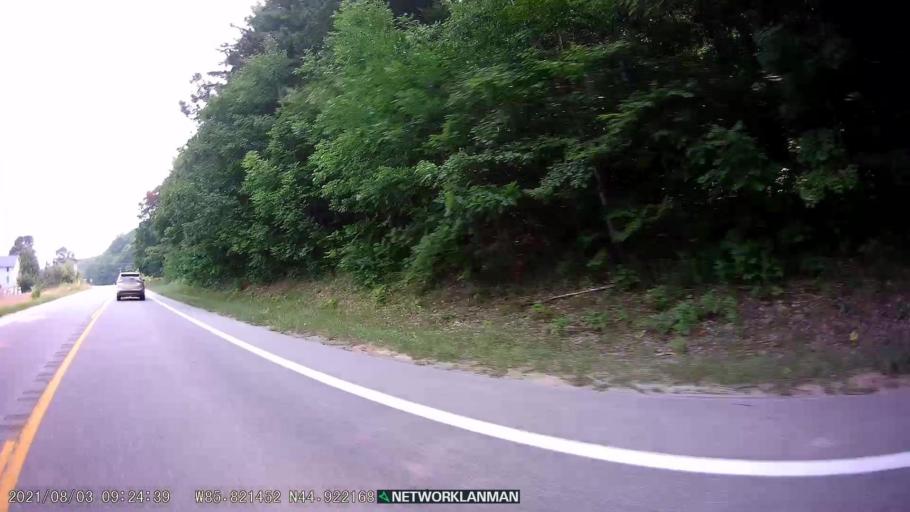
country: US
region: Michigan
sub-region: Leelanau County
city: Leland
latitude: 44.9223
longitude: -85.8213
